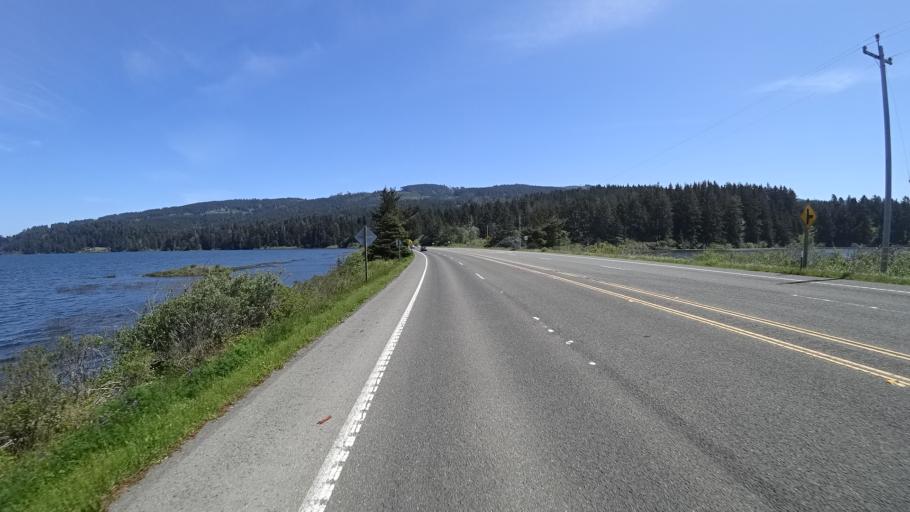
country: US
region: California
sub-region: Humboldt County
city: Westhaven-Moonstone
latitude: 41.1641
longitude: -124.1081
